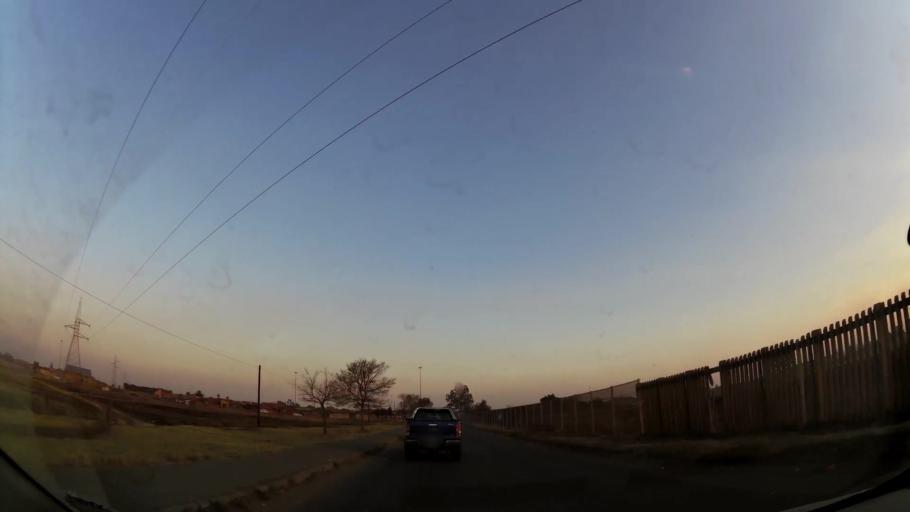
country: ZA
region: Gauteng
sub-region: Ekurhuleni Metropolitan Municipality
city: Springs
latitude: -26.2961
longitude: 28.4072
